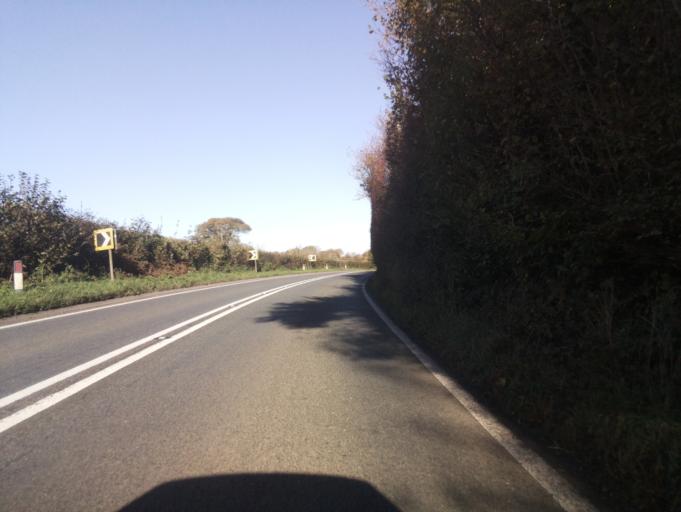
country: GB
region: England
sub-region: Somerset
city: Yeovil
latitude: 50.9087
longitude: -2.6250
